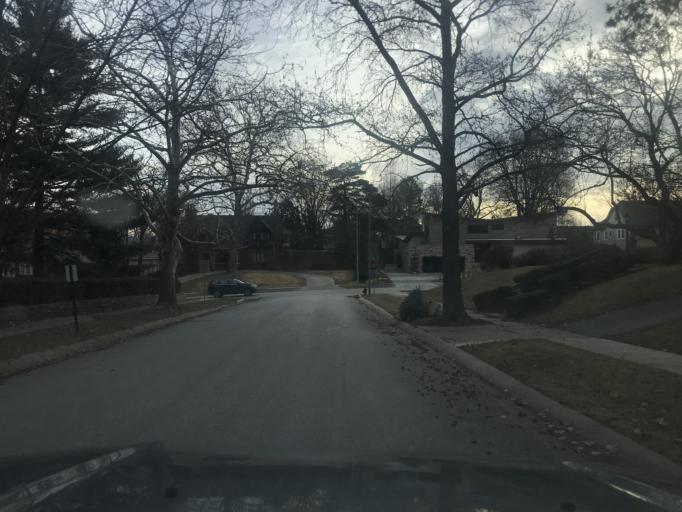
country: US
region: Kansas
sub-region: Johnson County
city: Mission Hills
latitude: 39.0233
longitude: -94.5934
